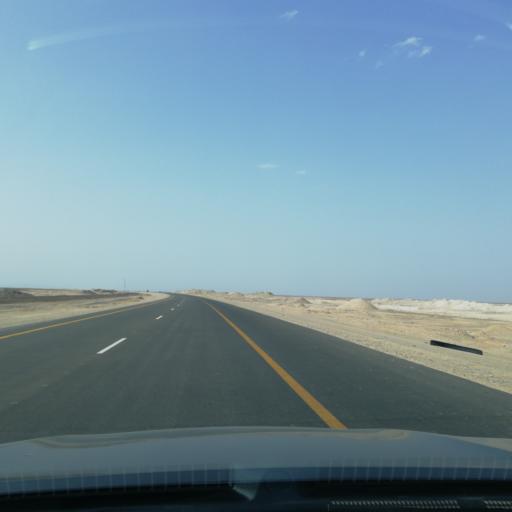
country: OM
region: Muhafazat ad Dakhiliyah
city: Adam
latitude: 22.1236
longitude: 57.5252
